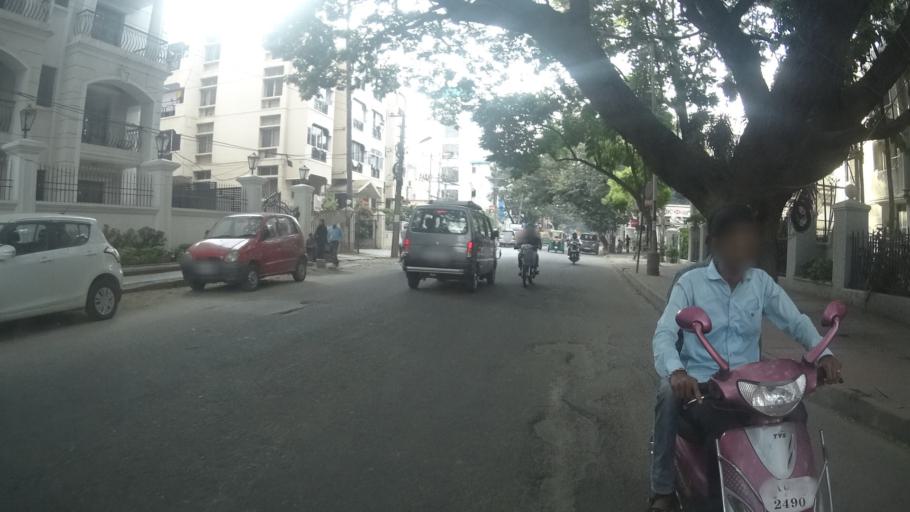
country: IN
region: Karnataka
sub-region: Bangalore Urban
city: Bangalore
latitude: 12.9949
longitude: 77.6149
